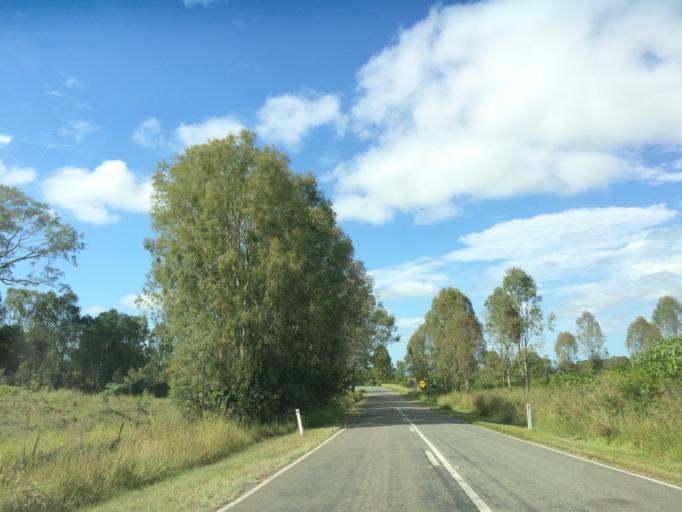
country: AU
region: Queensland
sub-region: Logan
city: Cedar Vale
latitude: -27.8889
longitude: 152.9735
